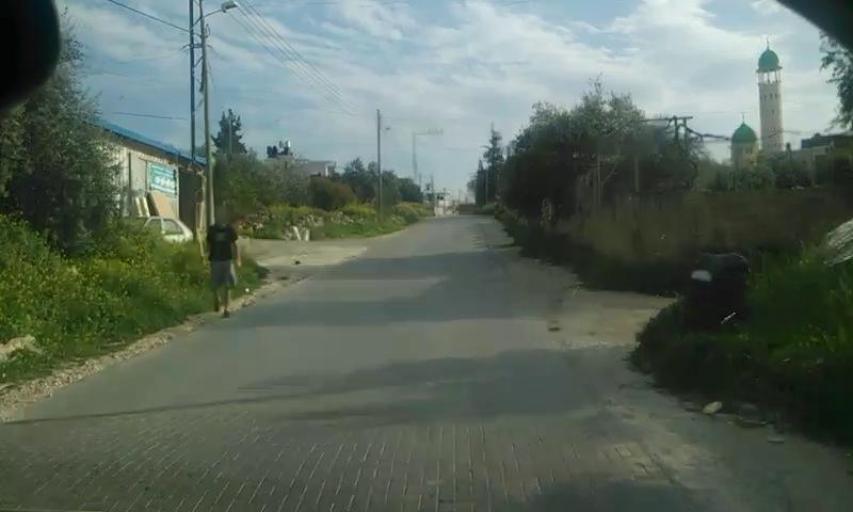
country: PS
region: West Bank
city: Nuba
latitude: 31.6115
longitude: 35.0342
